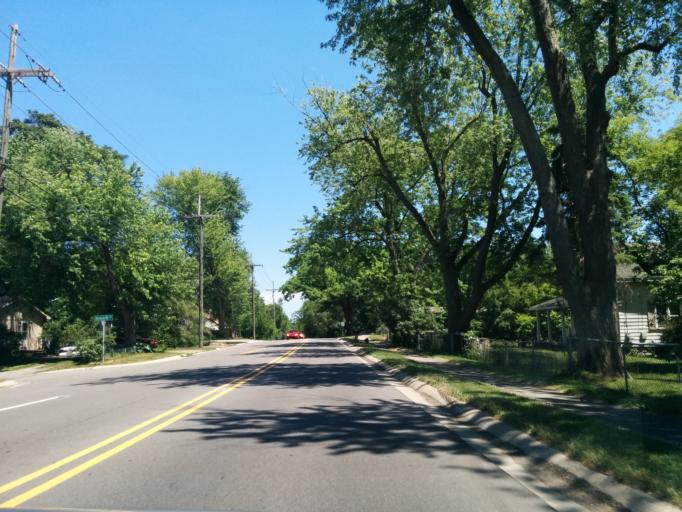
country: US
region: Michigan
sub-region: Oakland County
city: West Bloomfield Township
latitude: 42.5746
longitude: -83.4206
